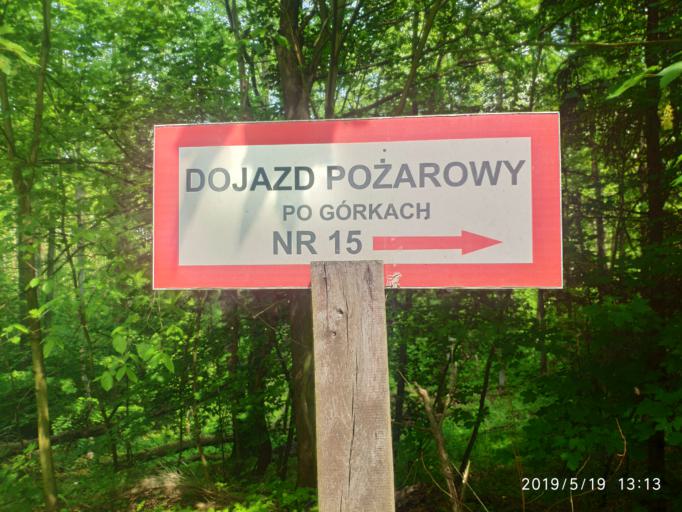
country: PL
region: Lubusz
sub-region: Powiat zielonogorski
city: Czerwiensk
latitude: 52.0326
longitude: 15.3119
